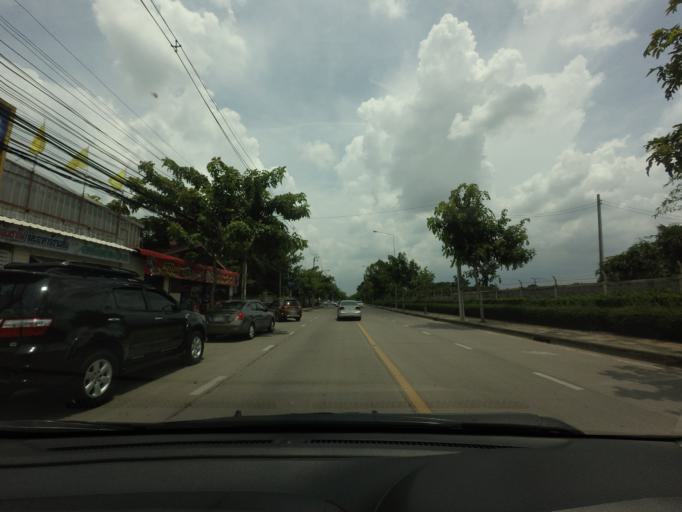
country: TH
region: Bangkok
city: Don Mueang
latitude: 13.9465
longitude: 100.5765
